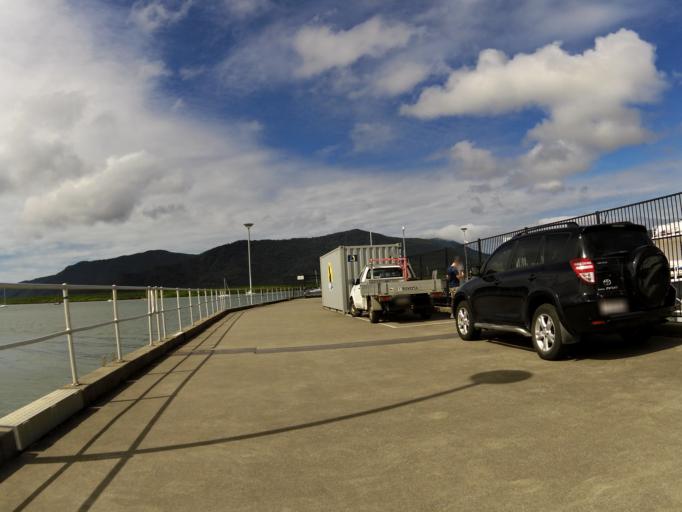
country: AU
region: Queensland
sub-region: Cairns
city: Cairns
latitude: -16.9171
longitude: 145.7829
